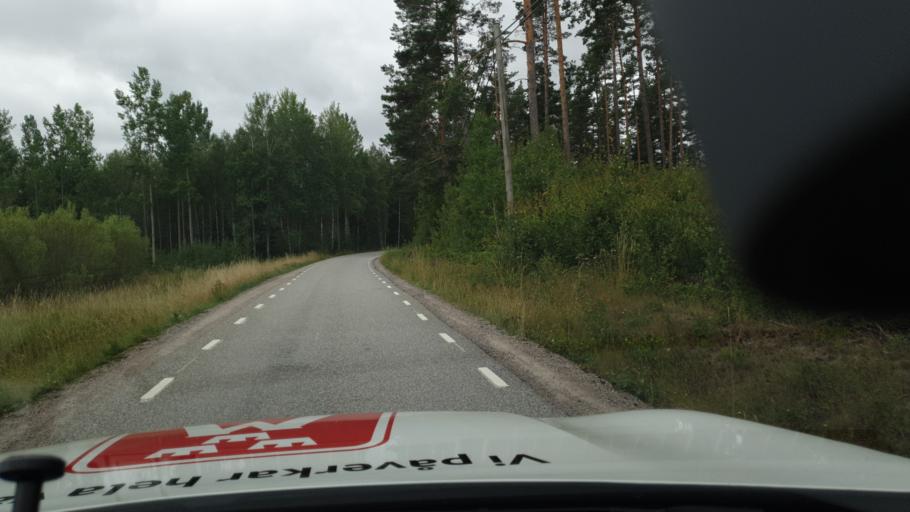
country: SE
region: Soedermanland
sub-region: Gnesta Kommun
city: Gnesta
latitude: 59.0390
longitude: 17.2414
